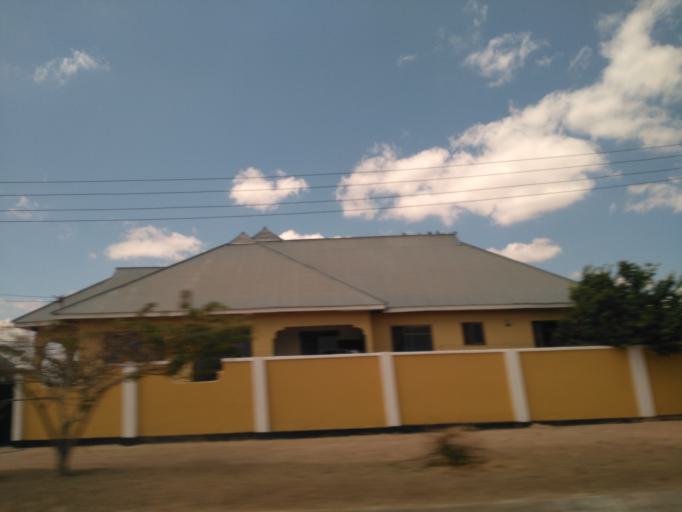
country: TZ
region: Dodoma
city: Kisasa
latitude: -6.1697
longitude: 35.7968
